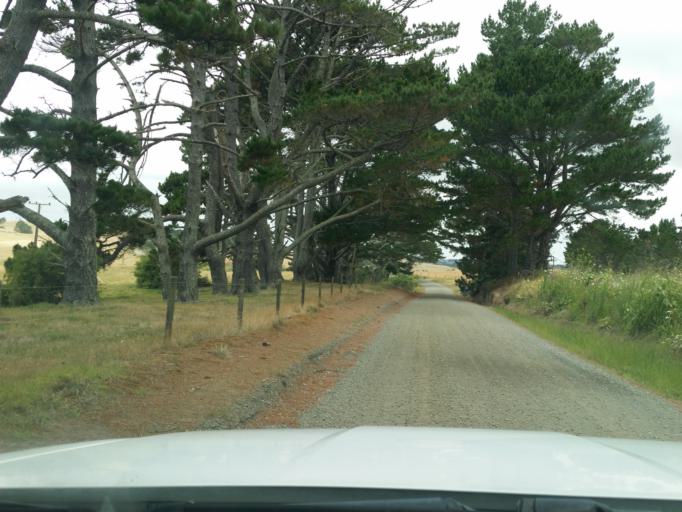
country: NZ
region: Northland
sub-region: Kaipara District
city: Dargaville
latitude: -35.9871
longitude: 173.8170
